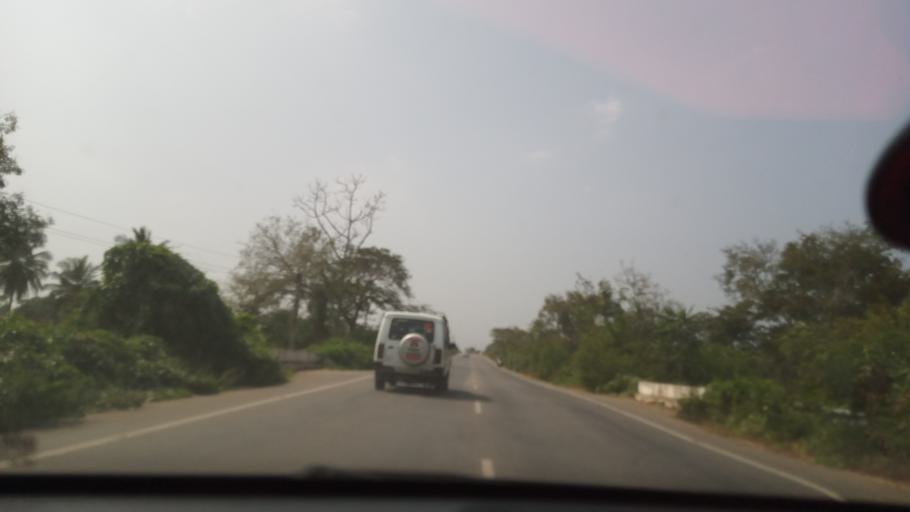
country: IN
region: Karnataka
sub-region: Chamrajnagar
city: Chamrajnagar
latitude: 11.9954
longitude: 76.8552
